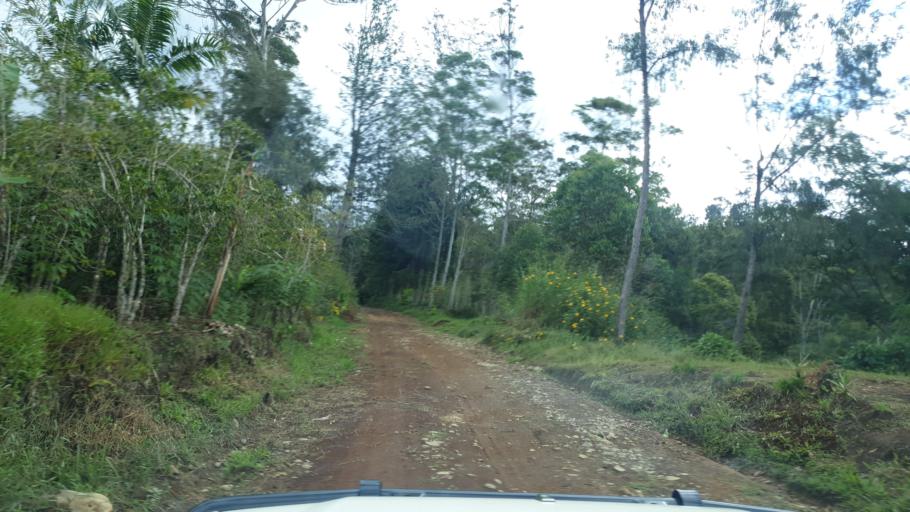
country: PG
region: Eastern Highlands
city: Goroka
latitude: -5.9210
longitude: 145.2630
